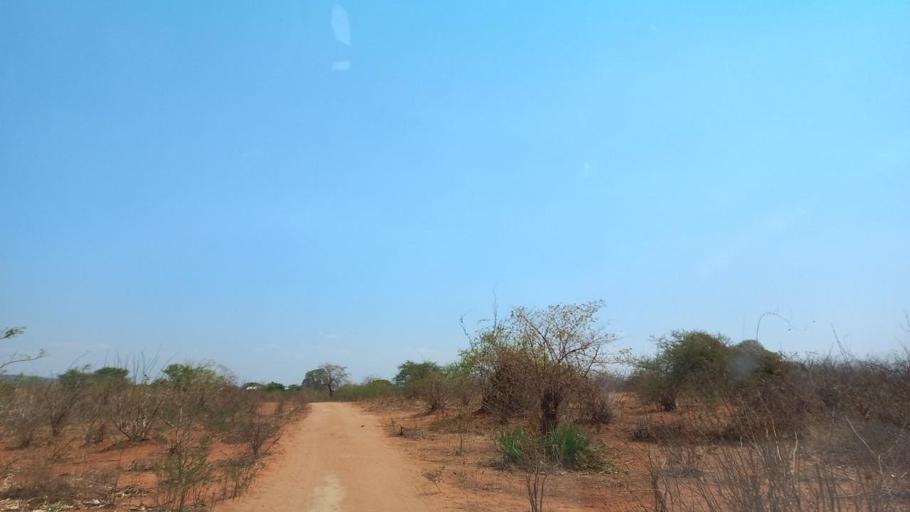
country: ZM
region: Lusaka
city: Luangwa
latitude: -15.5994
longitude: 30.4017
